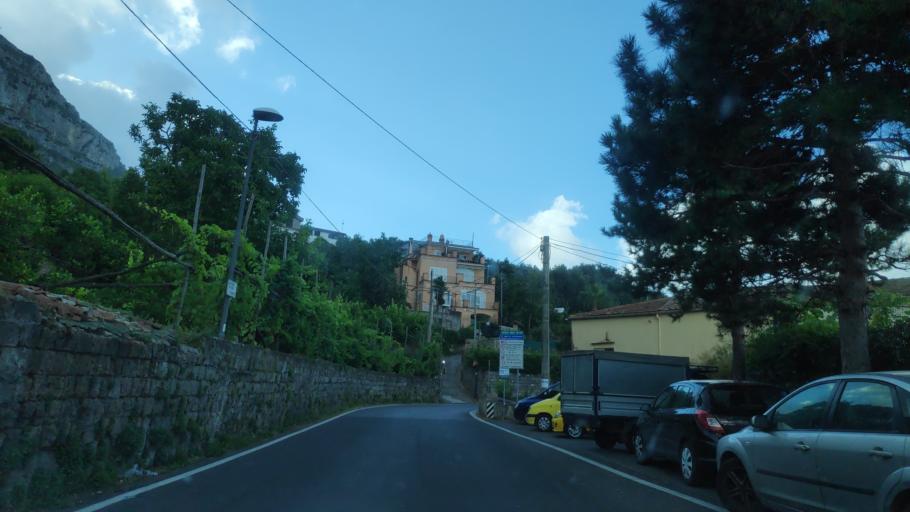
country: IT
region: Campania
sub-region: Provincia di Napoli
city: Piano di Sorrento
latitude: 40.6272
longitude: 14.4244
